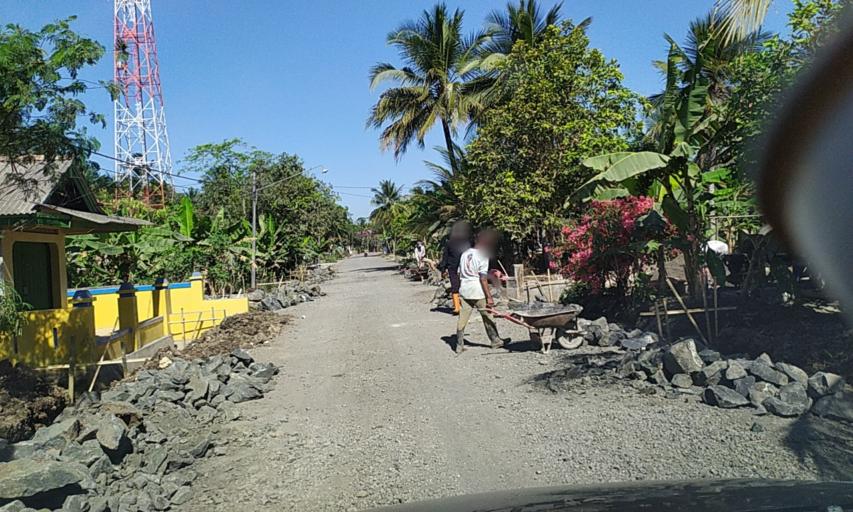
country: ID
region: Central Java
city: Kalenaren
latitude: -7.5746
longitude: 108.7785
